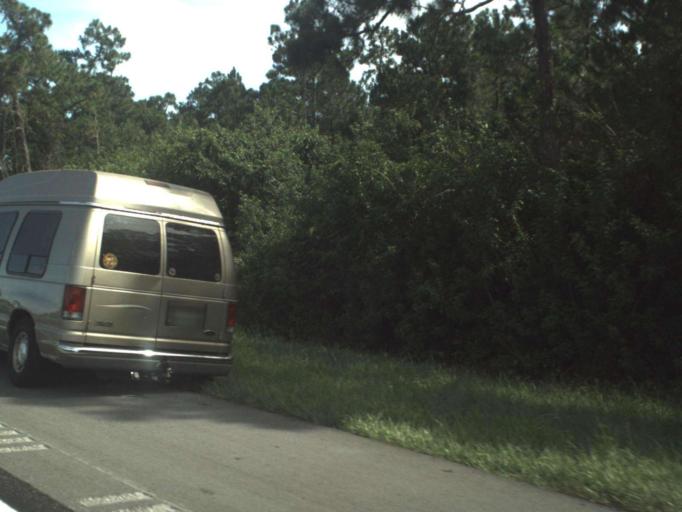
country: US
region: Florida
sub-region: Indian River County
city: West Vero Corridor
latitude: 27.5627
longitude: -80.4842
